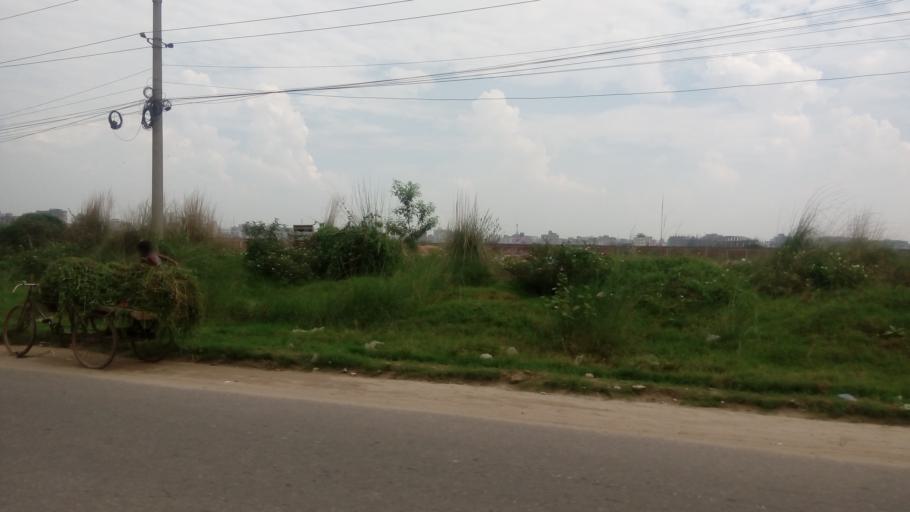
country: BD
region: Dhaka
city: Azimpur
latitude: 23.7476
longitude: 90.3526
